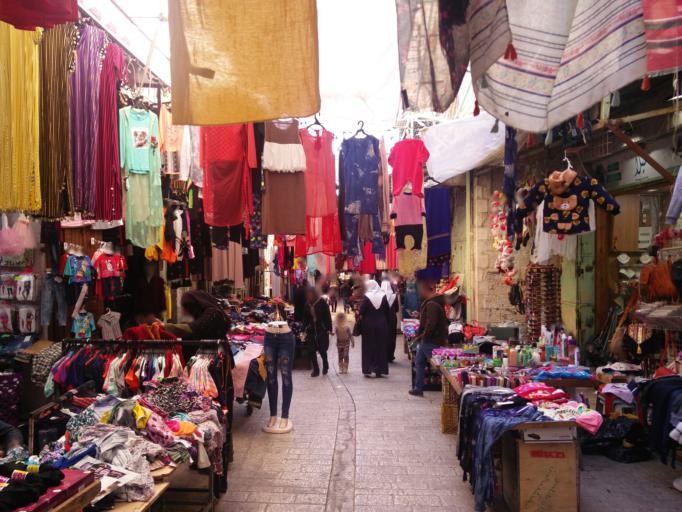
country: PS
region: West Bank
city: Hebron
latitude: 31.5264
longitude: 35.1041
